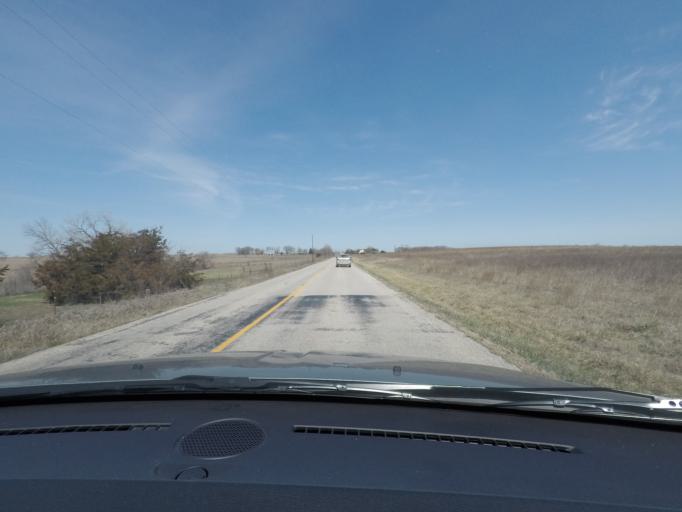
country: US
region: Kansas
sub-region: Lyon County
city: Emporia
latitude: 38.6227
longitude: -96.1696
